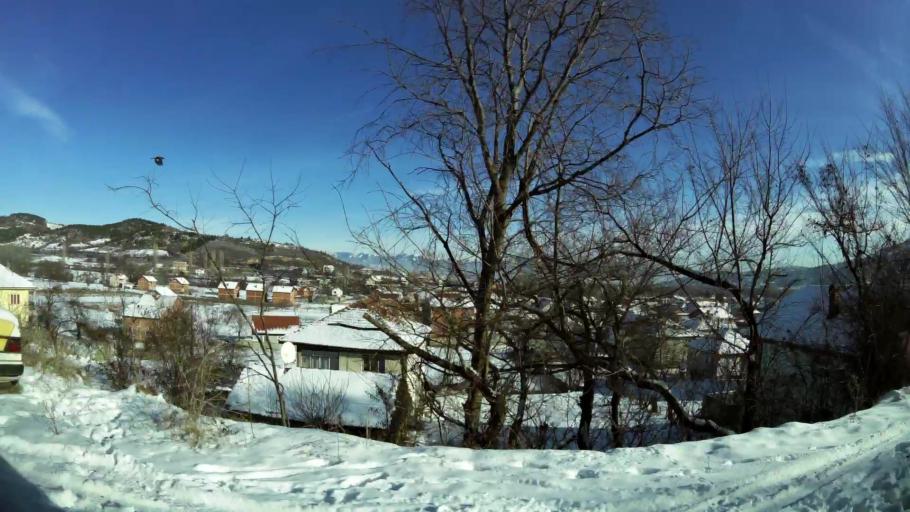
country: MK
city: Ljubin
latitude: 41.9803
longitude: 21.3024
